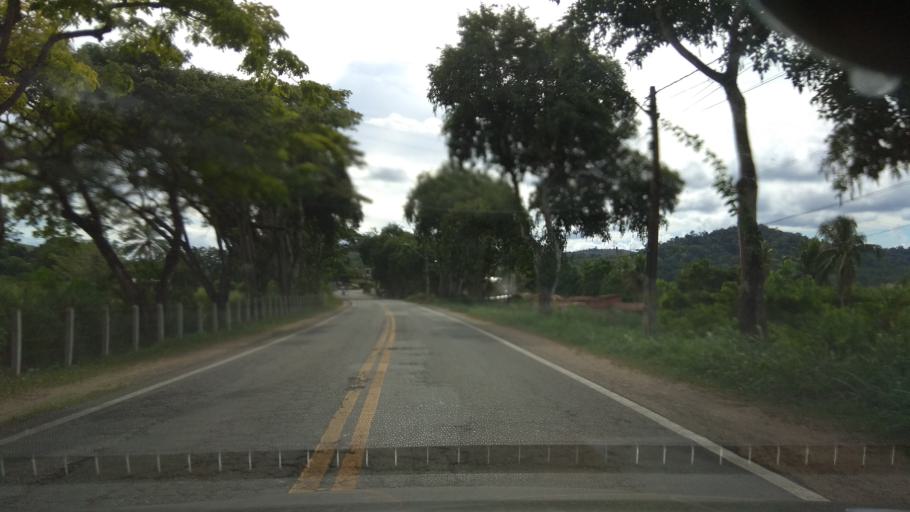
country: BR
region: Bahia
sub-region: Ubata
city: Ubata
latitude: -14.2009
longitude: -39.5338
